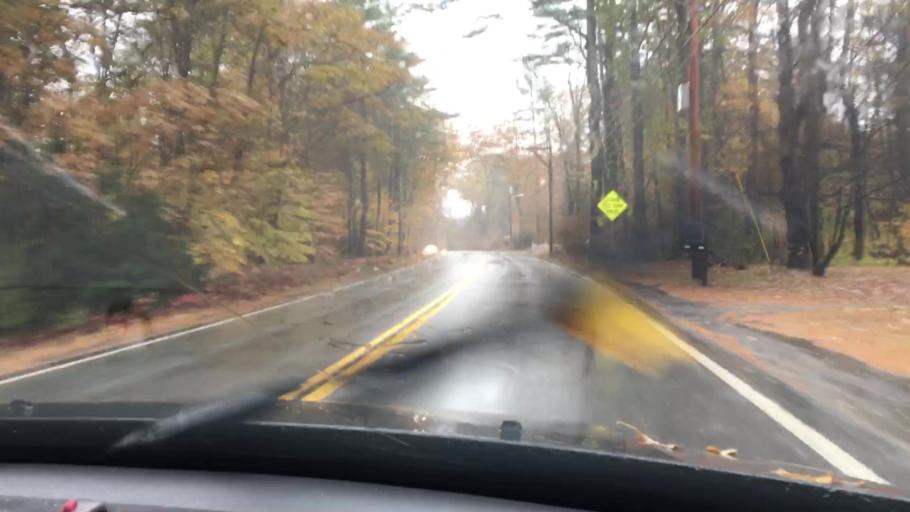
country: US
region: New Hampshire
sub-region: Belknap County
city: Meredith
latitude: 43.7045
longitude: -71.5205
